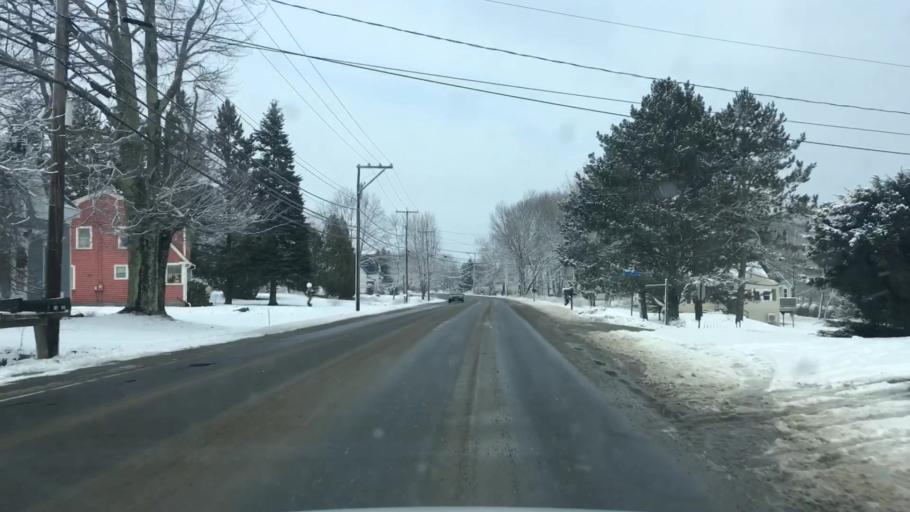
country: US
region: Maine
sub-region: Knox County
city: Rockland
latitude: 44.0807
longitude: -69.1057
